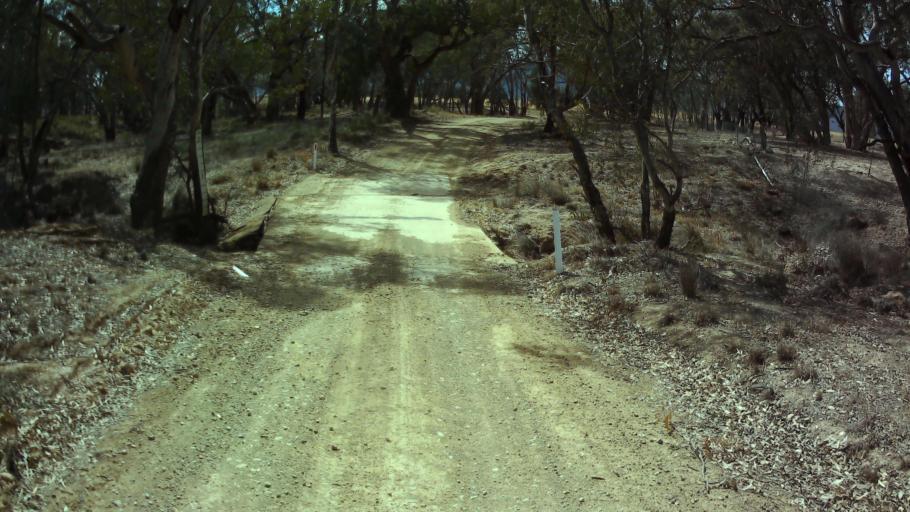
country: AU
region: New South Wales
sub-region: Weddin
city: Grenfell
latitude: -33.7202
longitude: 148.2529
